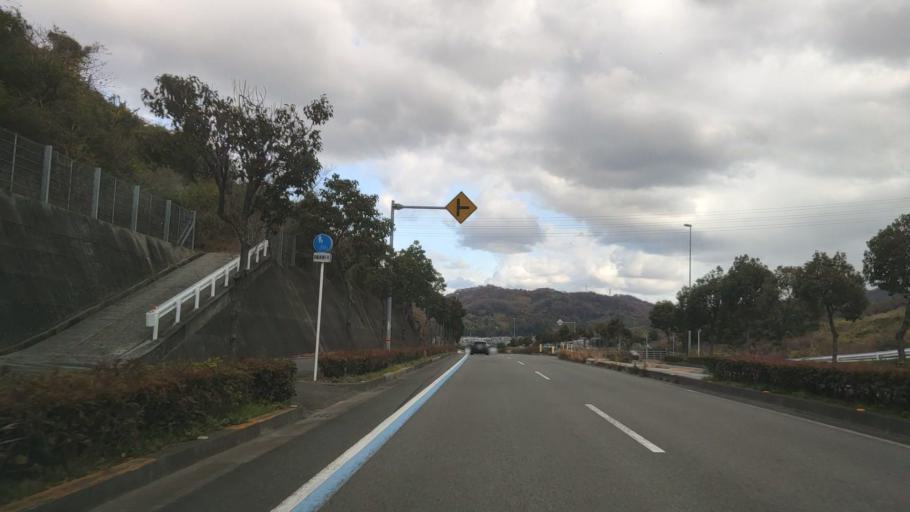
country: JP
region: Ehime
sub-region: Shikoku-chuo Shi
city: Matsuyama
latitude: 33.8913
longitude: 132.7573
